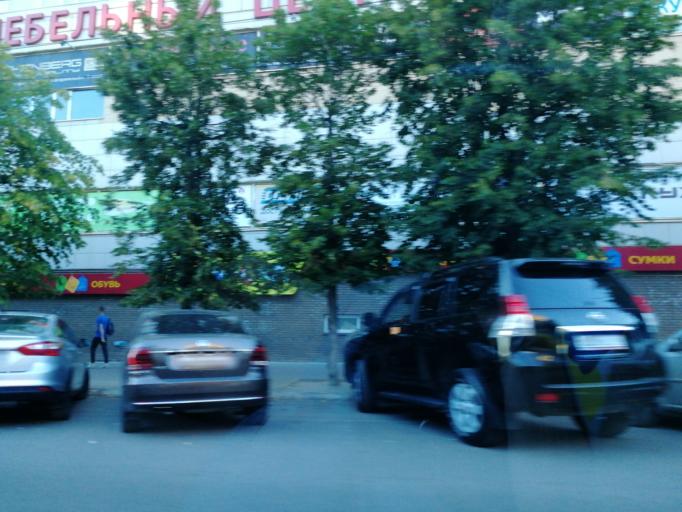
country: RU
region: Kaluga
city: Kaluga
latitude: 54.5153
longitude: 36.2422
